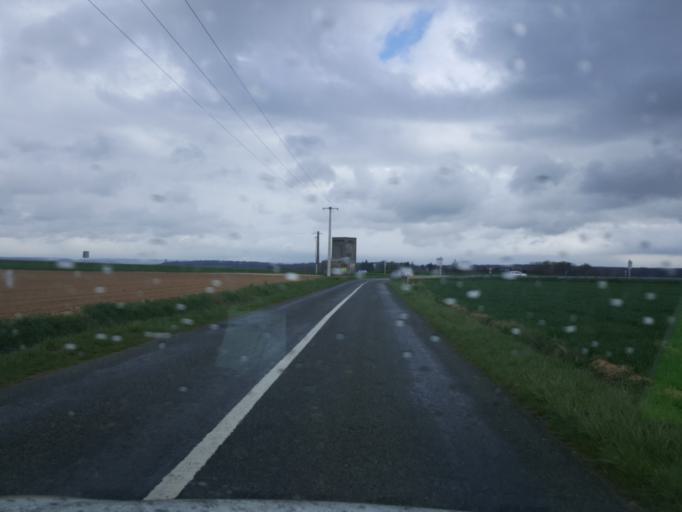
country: FR
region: Picardie
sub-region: Departement de l'Oise
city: Trie-Chateau
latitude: 49.2348
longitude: 1.8085
